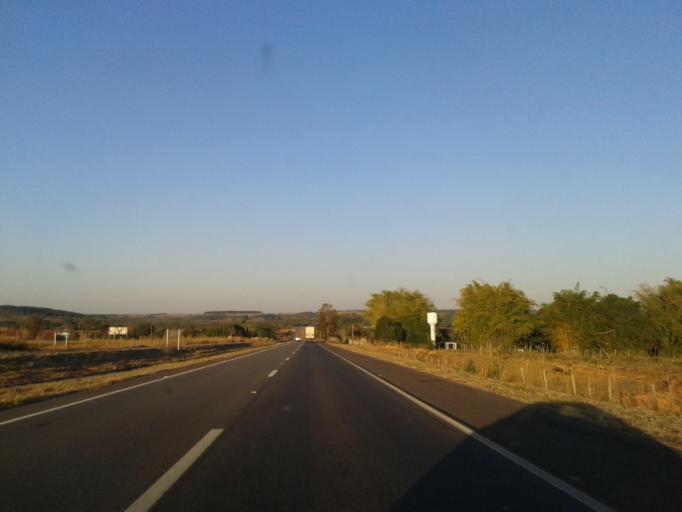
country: BR
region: Goias
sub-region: Goias
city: Goias
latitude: -16.0041
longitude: -50.0224
